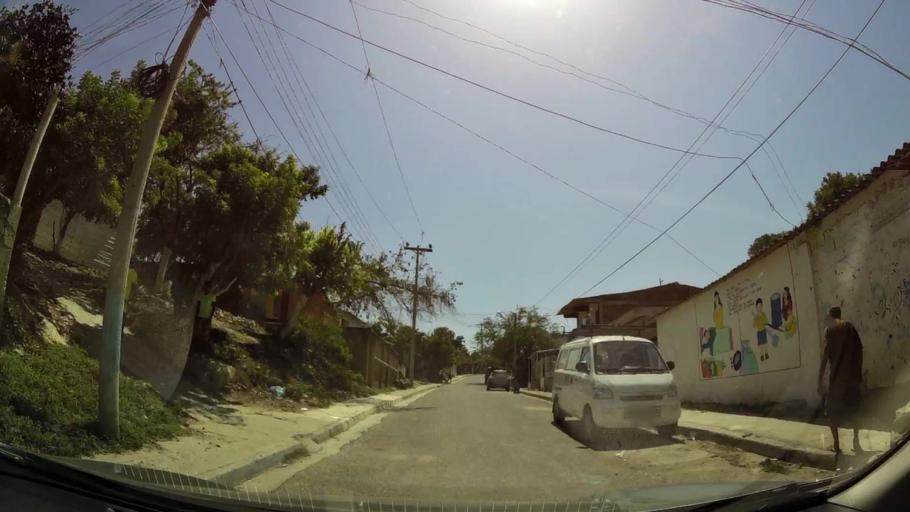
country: CO
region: Bolivar
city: Cartagena
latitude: 10.4288
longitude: -75.5260
